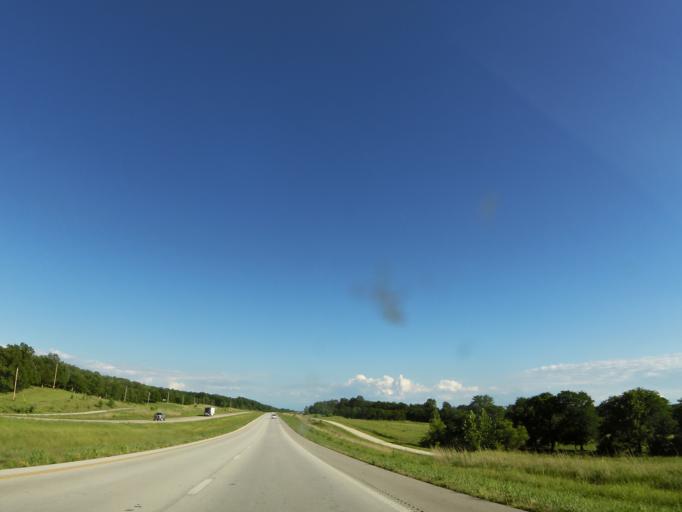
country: US
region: Missouri
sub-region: Pike County
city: Bowling Green
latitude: 39.4317
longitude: -91.2576
